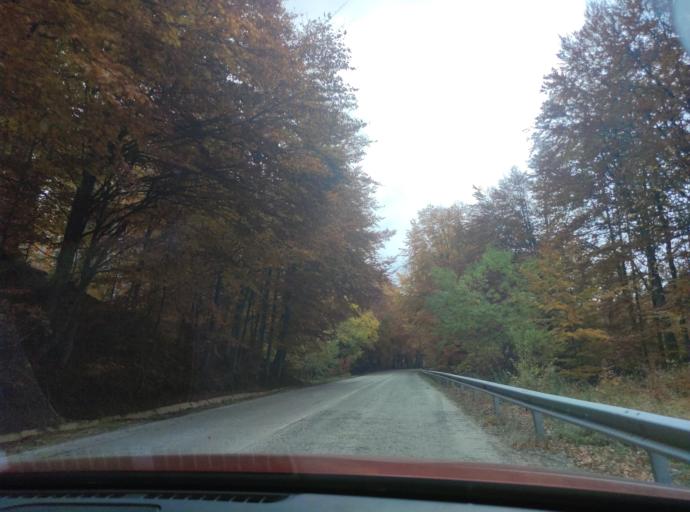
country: BG
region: Montana
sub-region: Obshtina Berkovitsa
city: Berkovitsa
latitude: 43.1172
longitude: 23.1161
